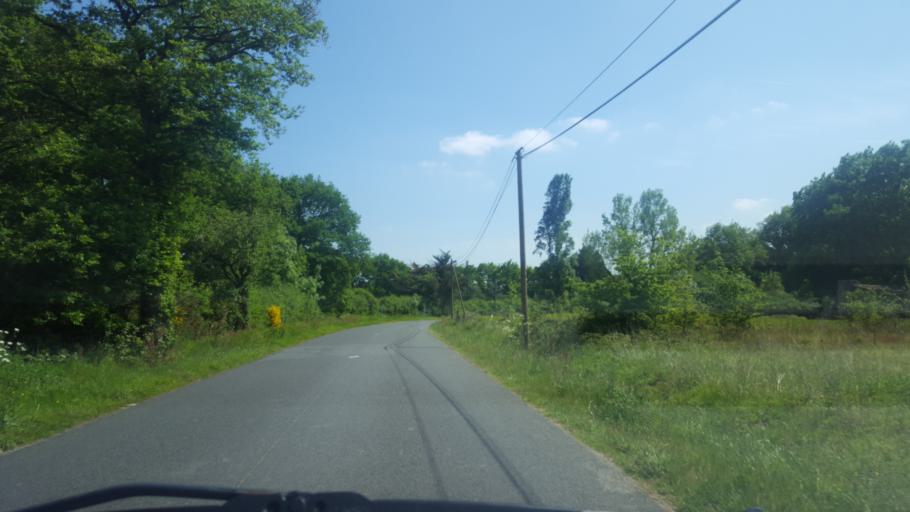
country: FR
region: Pays de la Loire
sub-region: Departement de la Loire-Atlantique
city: La Limouziniere
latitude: 47.0257
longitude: -1.5712
